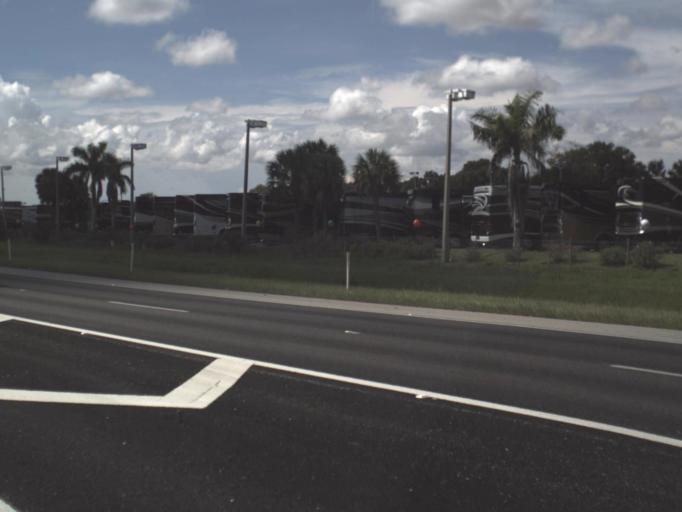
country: US
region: Florida
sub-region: Lee County
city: Tice
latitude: 26.6803
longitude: -81.7988
